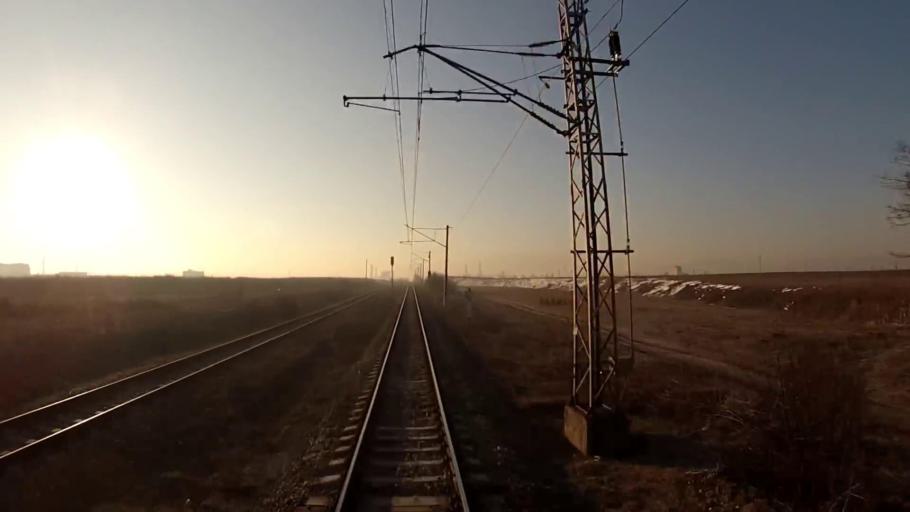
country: BG
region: Sofiya
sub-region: Obshtina Kostinbrod
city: Kostinbrod
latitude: 42.7962
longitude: 23.2071
